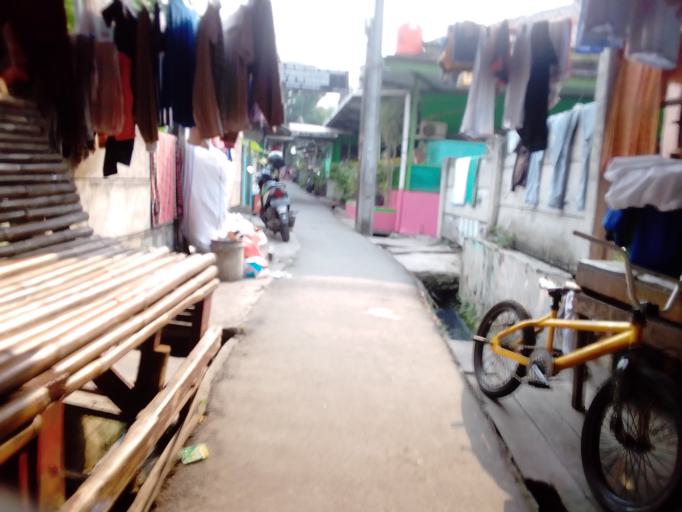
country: ID
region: Jakarta Raya
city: Jakarta
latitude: -6.1998
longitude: 106.8166
